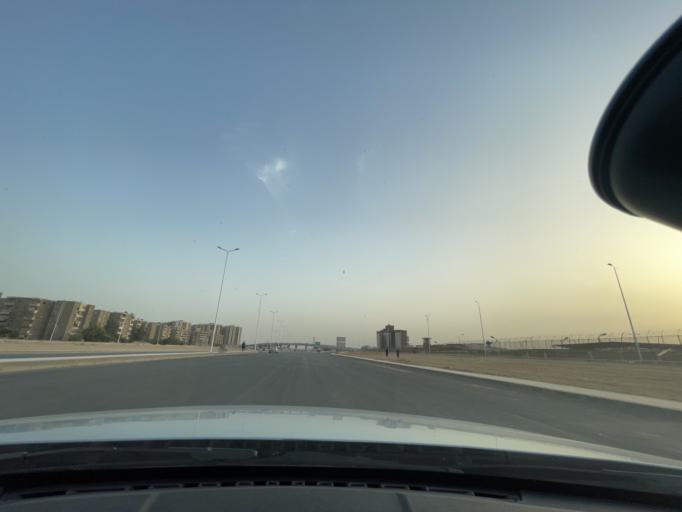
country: EG
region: Muhafazat al Qahirah
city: Cairo
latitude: 30.0397
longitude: 31.3583
